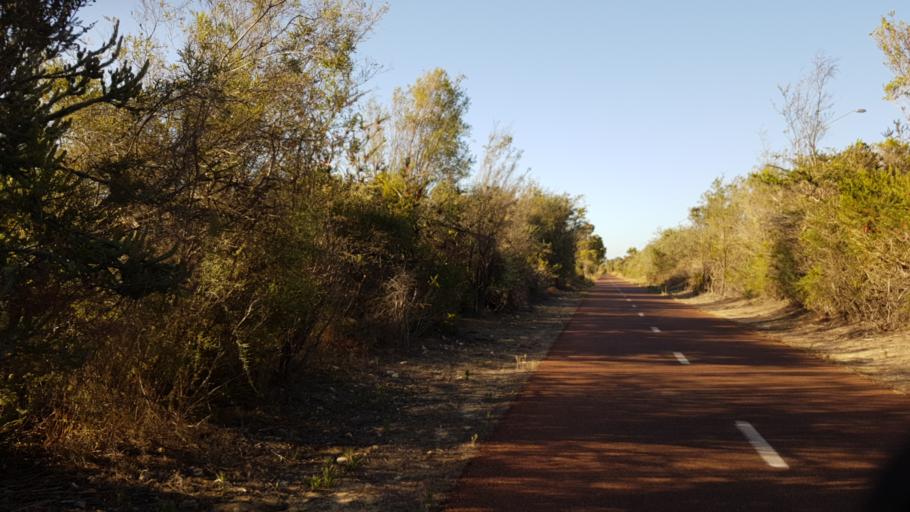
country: AU
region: Western Australia
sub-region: Kwinana
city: Bertram
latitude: -32.2511
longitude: 115.8523
